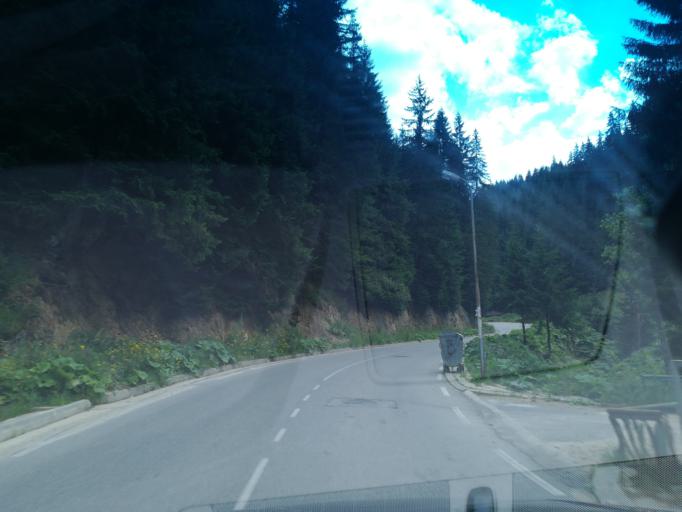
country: BG
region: Smolyan
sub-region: Obshtina Chepelare
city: Chepelare
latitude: 41.6591
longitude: 24.6328
